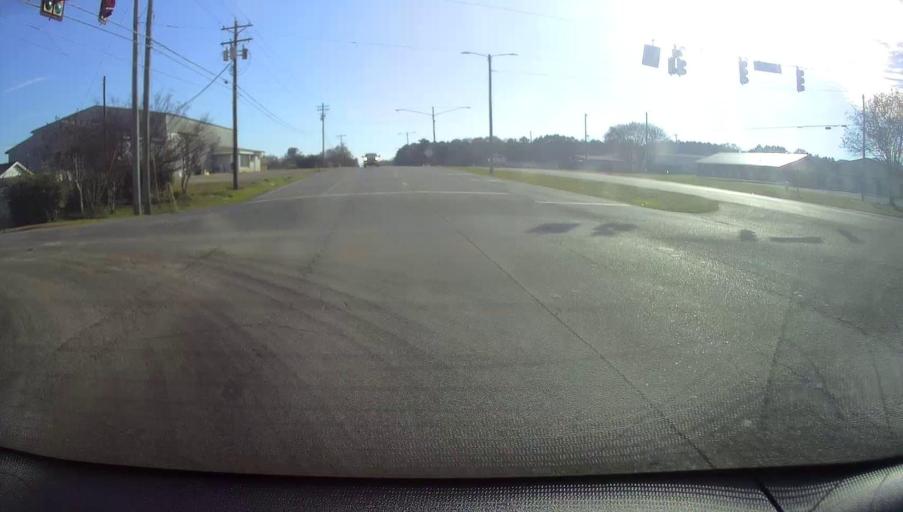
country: US
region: Alabama
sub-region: Limestone County
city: Athens
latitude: 34.7748
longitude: -86.9570
